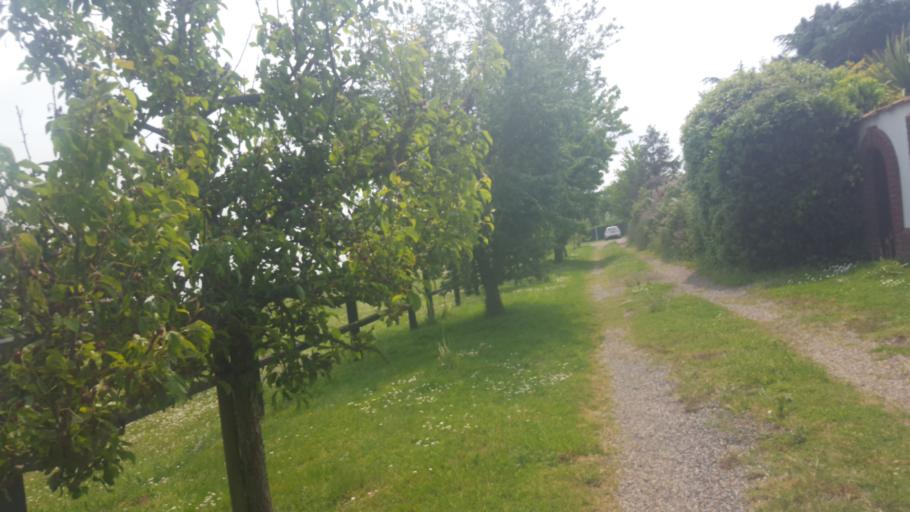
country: GB
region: England
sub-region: Essex
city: Saint Osyth
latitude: 51.7945
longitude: 1.0937
